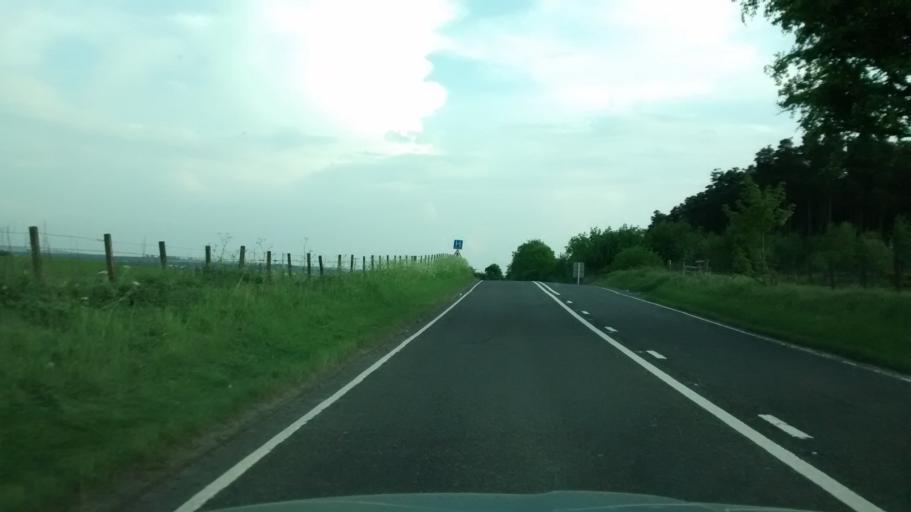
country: GB
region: Scotland
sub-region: West Lothian
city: Whitburn
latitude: 55.8787
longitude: -3.6859
